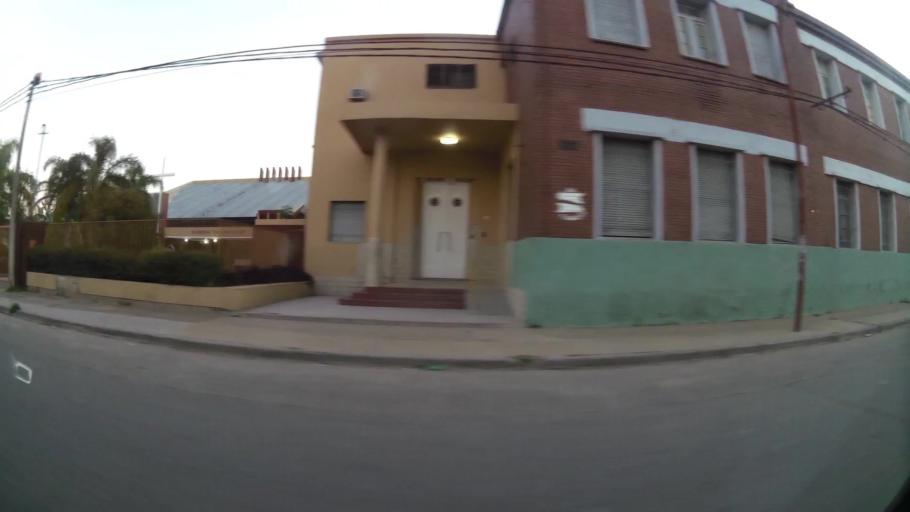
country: AR
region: Santa Fe
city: Santa Fe de la Vera Cruz
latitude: -31.6034
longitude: -60.7040
